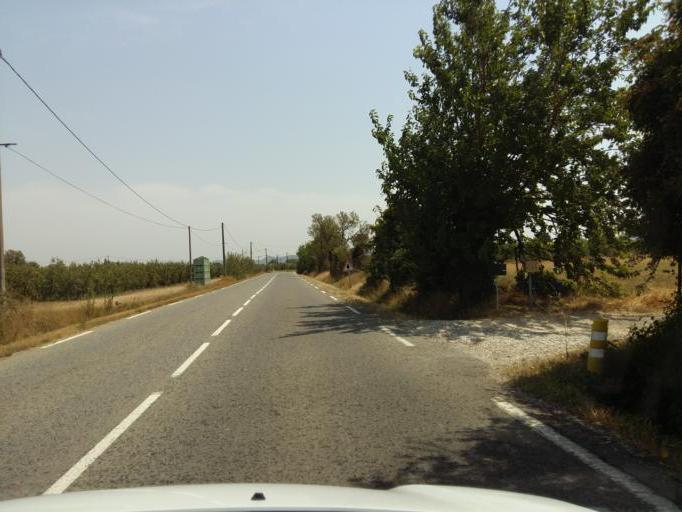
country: FR
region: Languedoc-Roussillon
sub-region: Departement du Gard
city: Pont-Saint-Esprit
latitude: 44.2578
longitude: 4.6705
